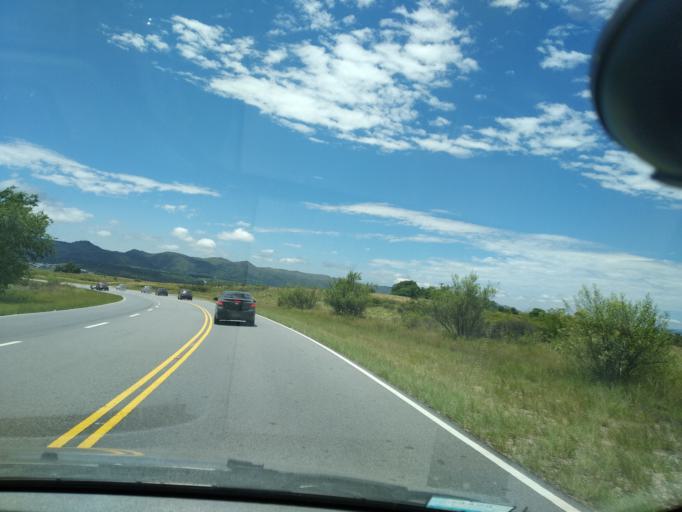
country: AR
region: Cordoba
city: Cuesta Blanca
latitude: -31.5869
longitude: -64.6193
